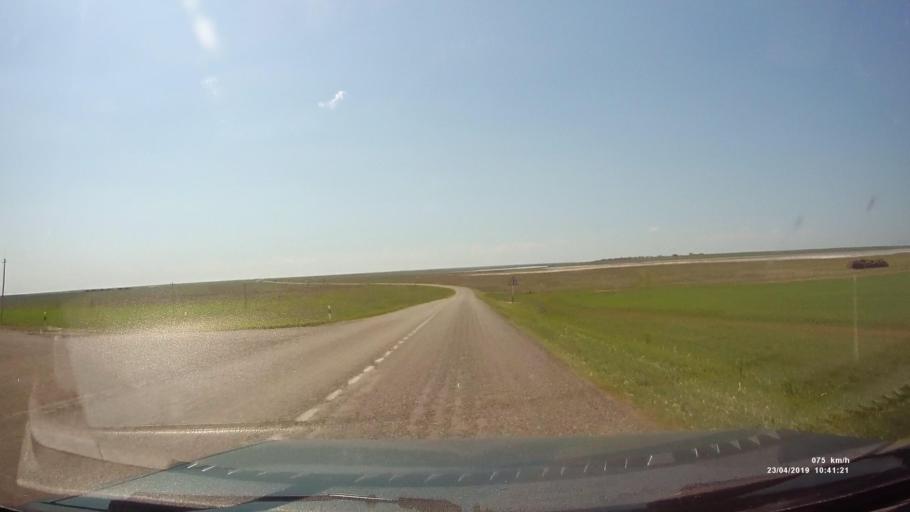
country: RU
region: Kalmykiya
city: Yashalta
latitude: 46.4949
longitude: 42.6380
